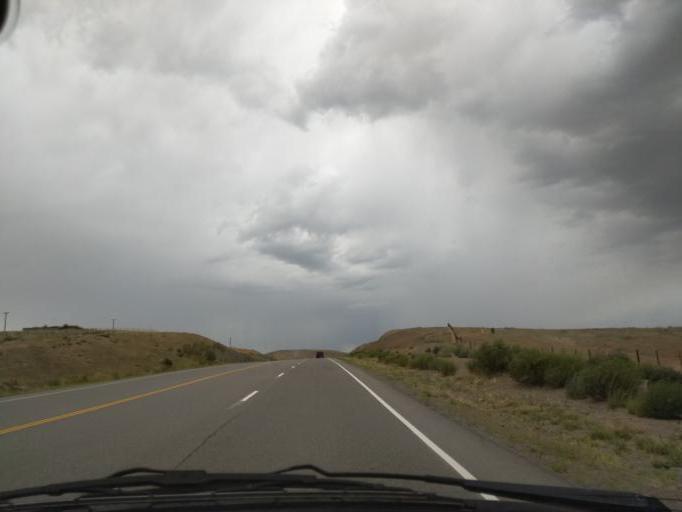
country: US
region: Colorado
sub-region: Delta County
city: Orchard City
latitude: 38.7973
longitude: -107.9154
